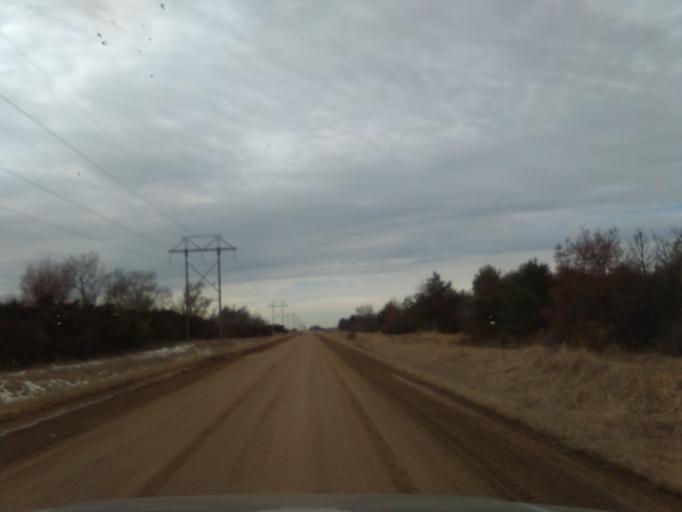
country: US
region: Nebraska
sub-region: Buffalo County
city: Gibbon
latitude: 40.6549
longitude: -98.7758
